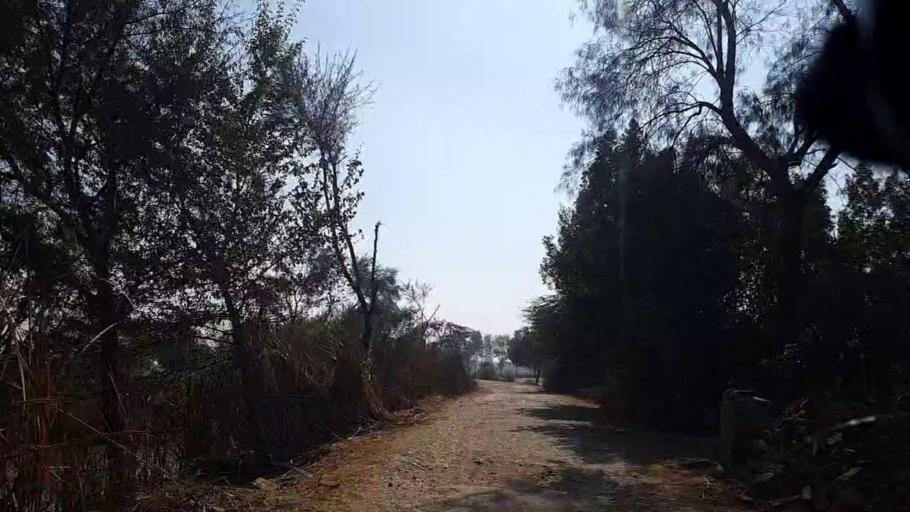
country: PK
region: Sindh
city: Khanpur
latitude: 27.7750
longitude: 69.4228
